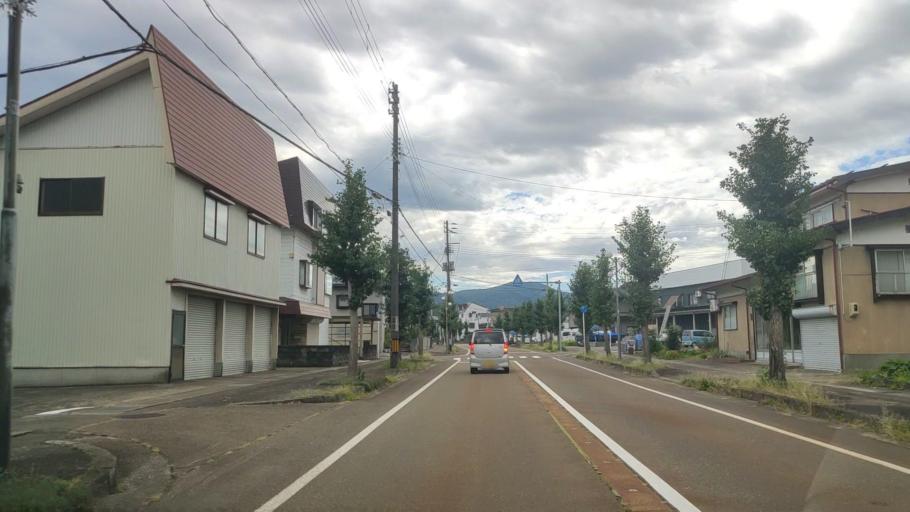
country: JP
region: Niigata
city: Arai
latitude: 37.0226
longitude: 138.2464
